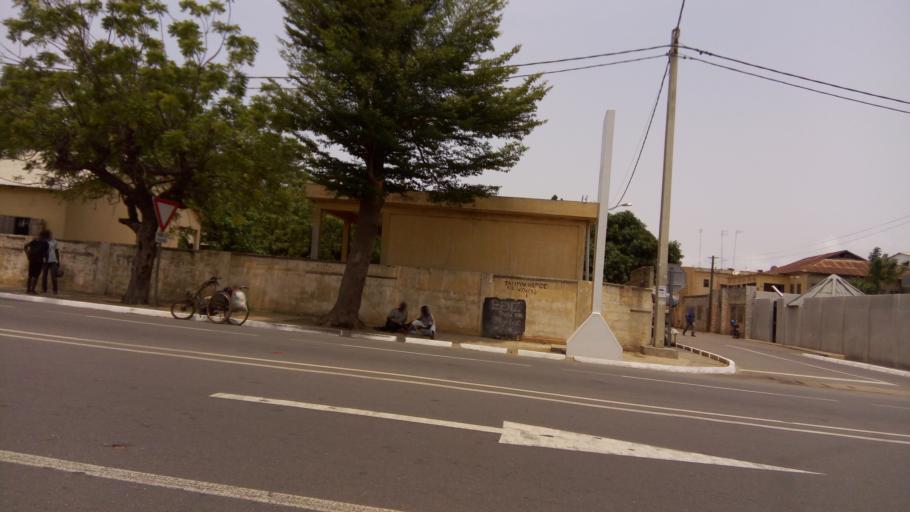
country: TG
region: Maritime
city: Lome
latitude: 6.1377
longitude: 1.2219
